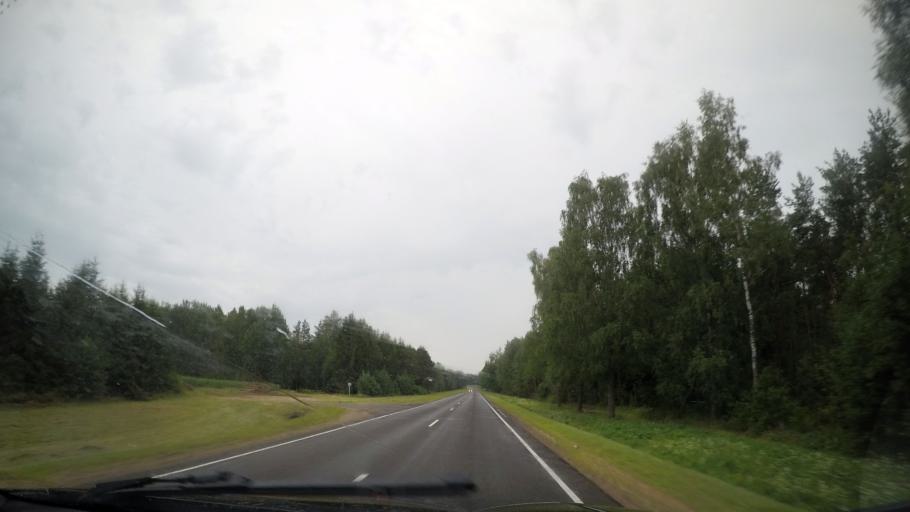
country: BY
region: Grodnenskaya
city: Hal'shany
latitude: 54.1383
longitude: 25.9166
